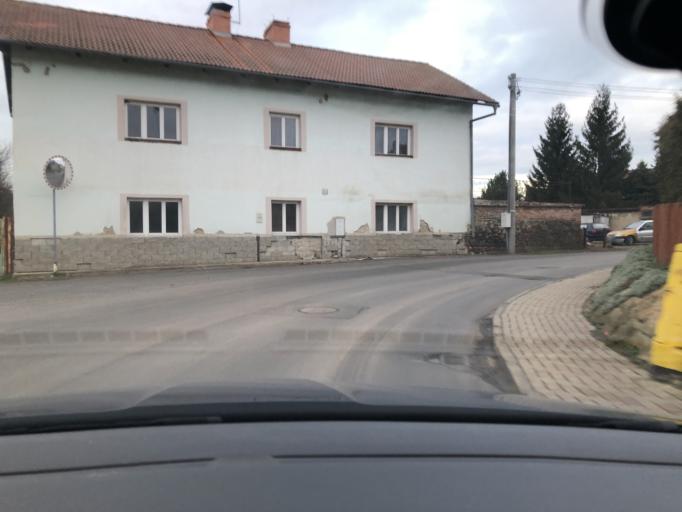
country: CZ
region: Ustecky
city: Rehlovice
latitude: 50.6075
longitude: 13.9503
